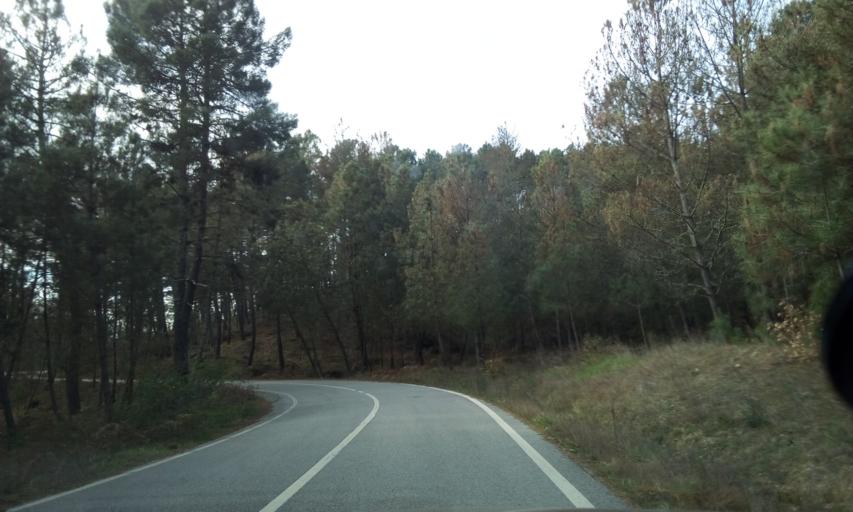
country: PT
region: Guarda
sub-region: Fornos de Algodres
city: Fornos de Algodres
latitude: 40.7188
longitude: -7.5594
